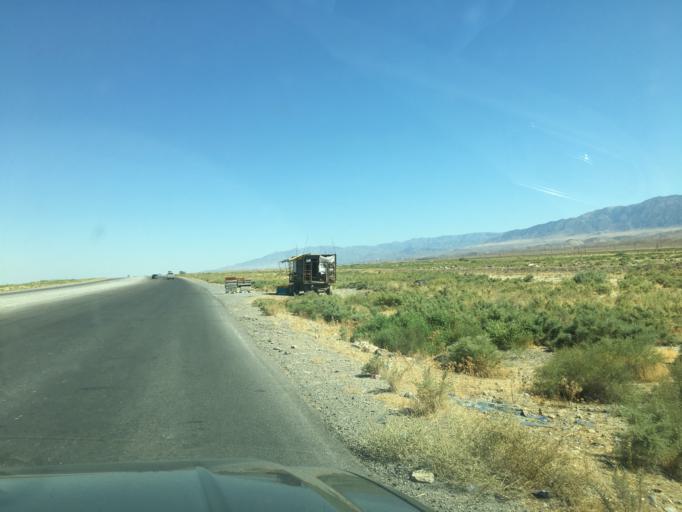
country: TM
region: Balkan
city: Serdar
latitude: 38.7679
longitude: 56.7400
